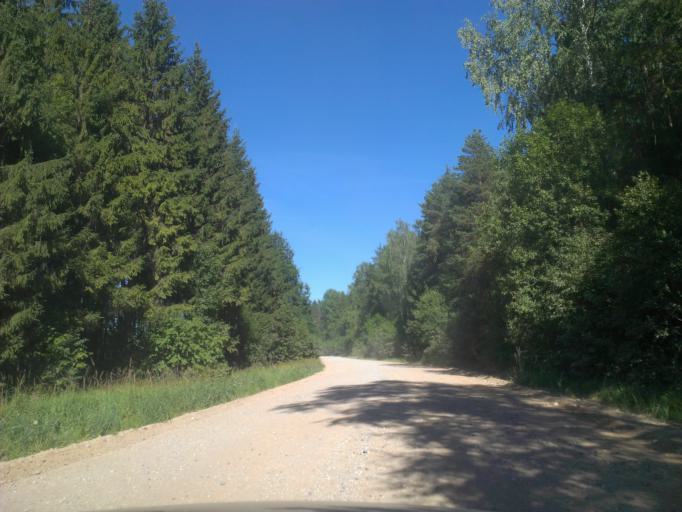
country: LV
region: Malpils
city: Malpils
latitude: 57.0546
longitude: 25.1273
